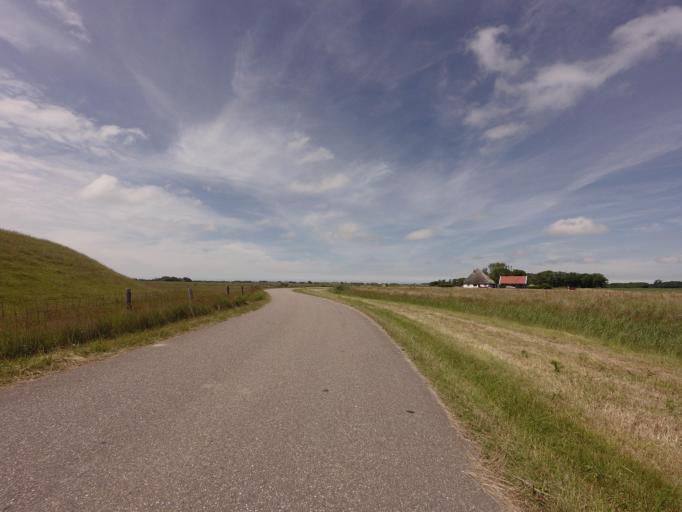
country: NL
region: North Holland
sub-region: Gemeente Texel
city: Den Burg
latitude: 53.0738
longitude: 4.8861
